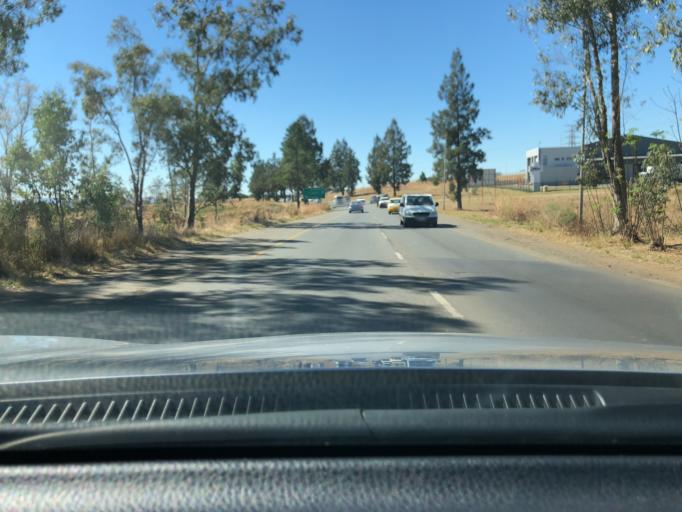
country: ZA
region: KwaZulu-Natal
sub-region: Amajuba District Municipality
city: Newcastle
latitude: -27.7616
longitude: 29.9576
